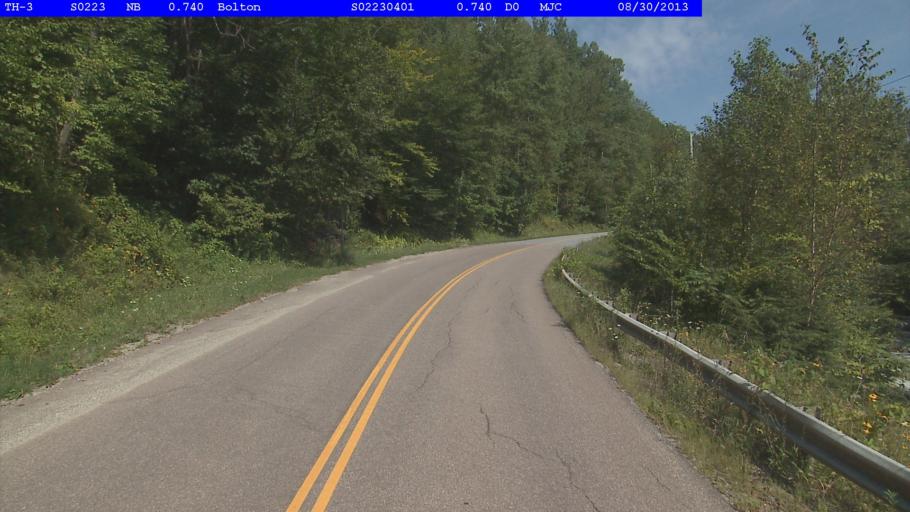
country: US
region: Vermont
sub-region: Washington County
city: Waterbury
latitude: 44.3815
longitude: -72.8751
